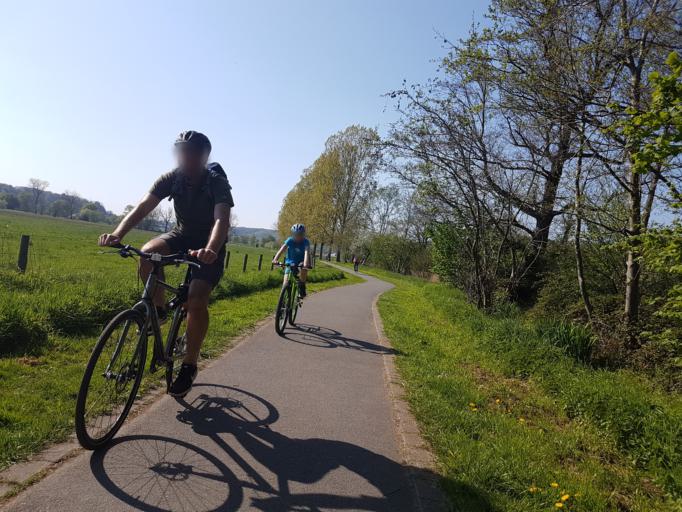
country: DE
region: North Rhine-Westphalia
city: Hattingen
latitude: 51.4151
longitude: 7.2307
